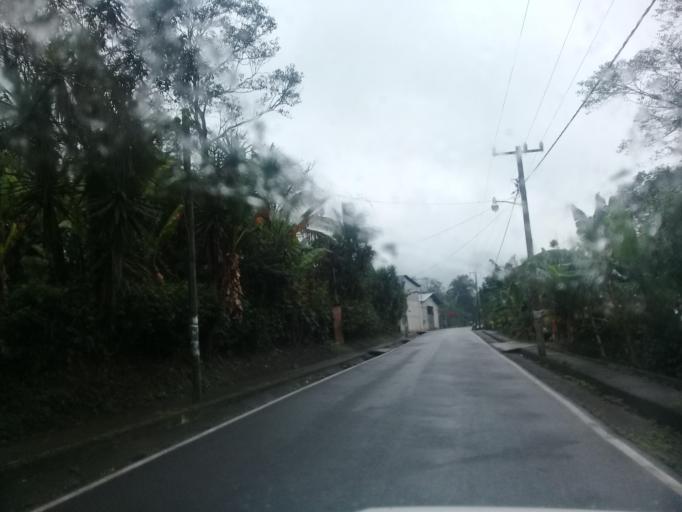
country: MX
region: Veracruz
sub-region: Amatlan de los Reyes
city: Centro de Readaptacion Social
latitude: 18.8041
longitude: -96.9532
